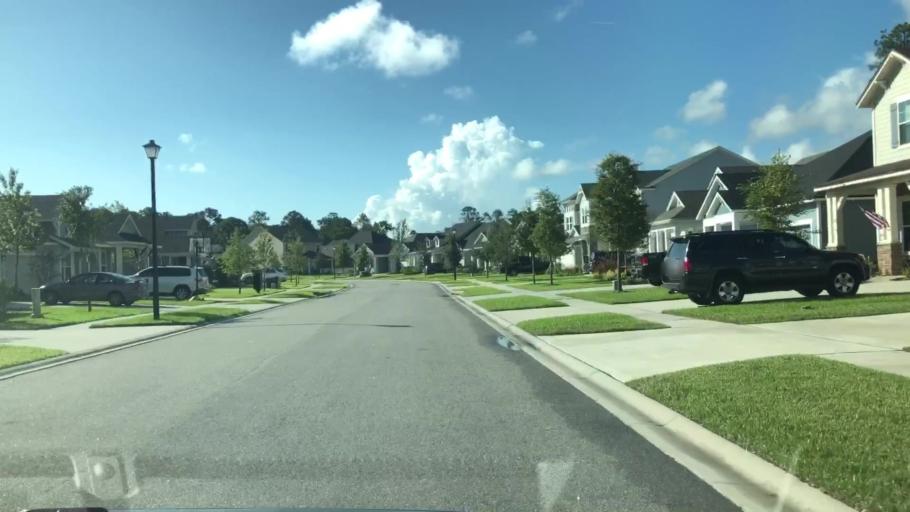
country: US
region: Florida
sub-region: Saint Johns County
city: Palm Valley
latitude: 30.1265
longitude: -81.4102
